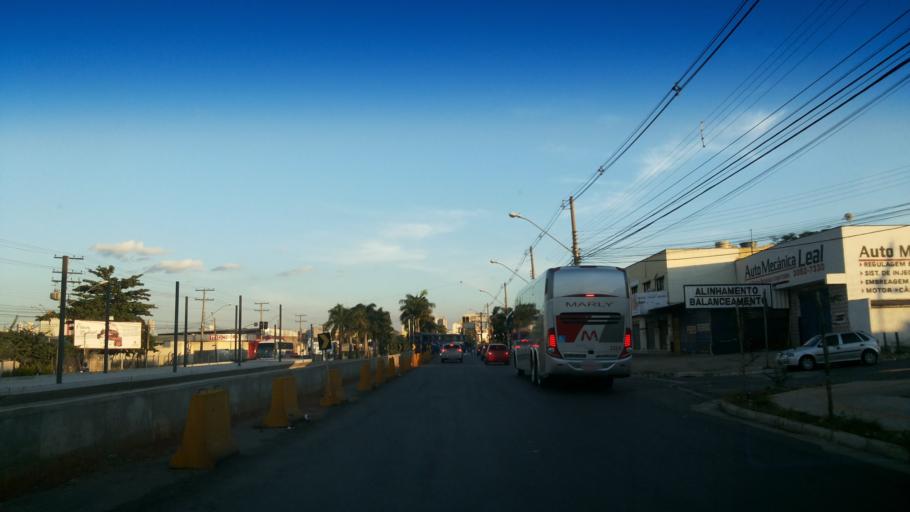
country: BR
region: Goias
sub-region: Goiania
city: Goiania
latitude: -16.6504
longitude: -49.2644
